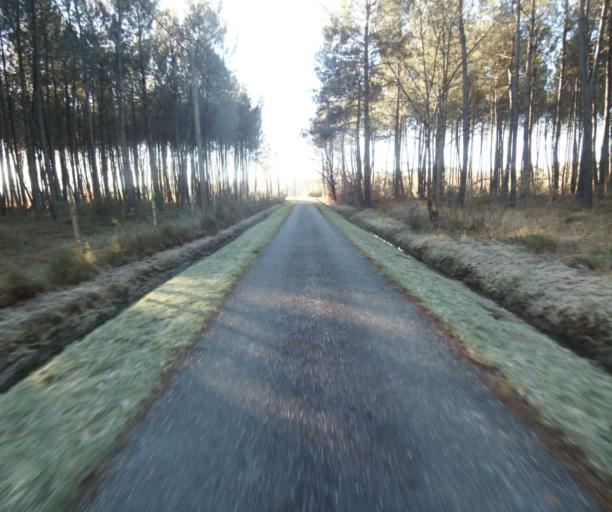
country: FR
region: Aquitaine
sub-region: Departement des Landes
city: Gabarret
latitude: 44.1099
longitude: 0.0588
